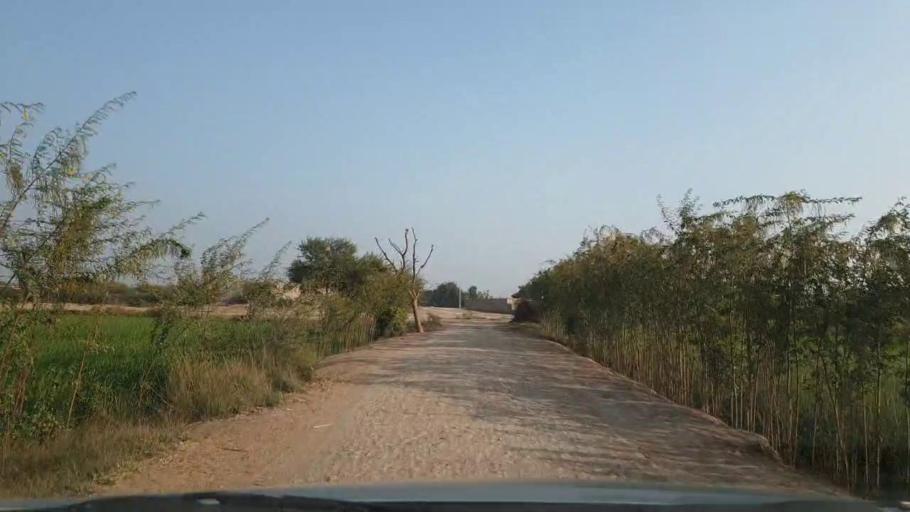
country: PK
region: Sindh
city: Tando Adam
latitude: 25.6706
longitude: 68.6465
